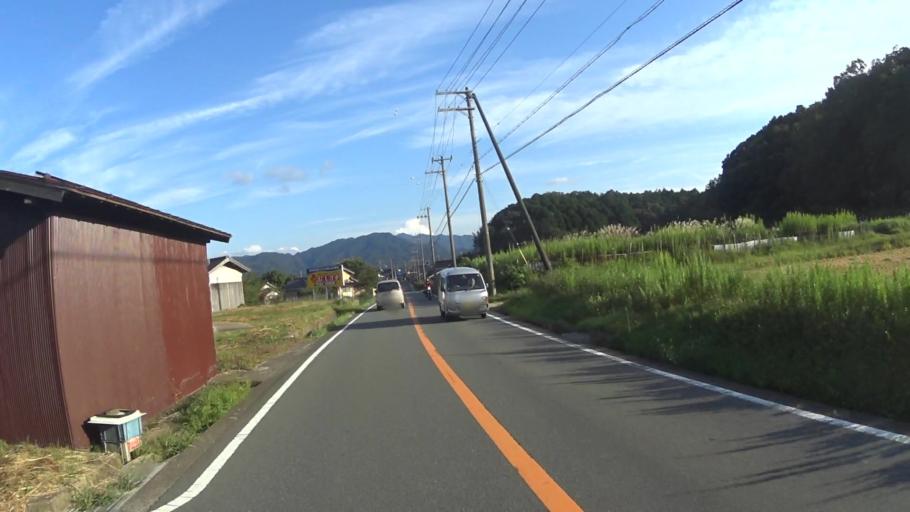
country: JP
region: Hyogo
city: Toyooka
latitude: 35.5919
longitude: 134.9227
